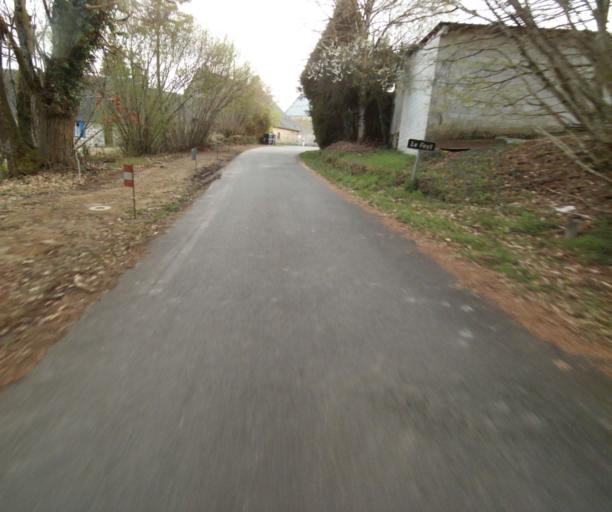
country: FR
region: Limousin
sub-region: Departement de la Correze
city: Correze
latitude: 45.2453
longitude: 1.9516
